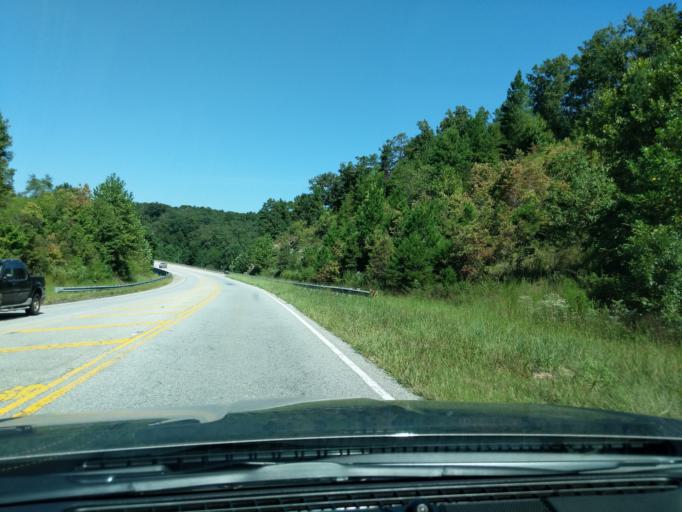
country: US
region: Georgia
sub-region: Habersham County
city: Demorest
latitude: 34.5716
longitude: -83.5880
